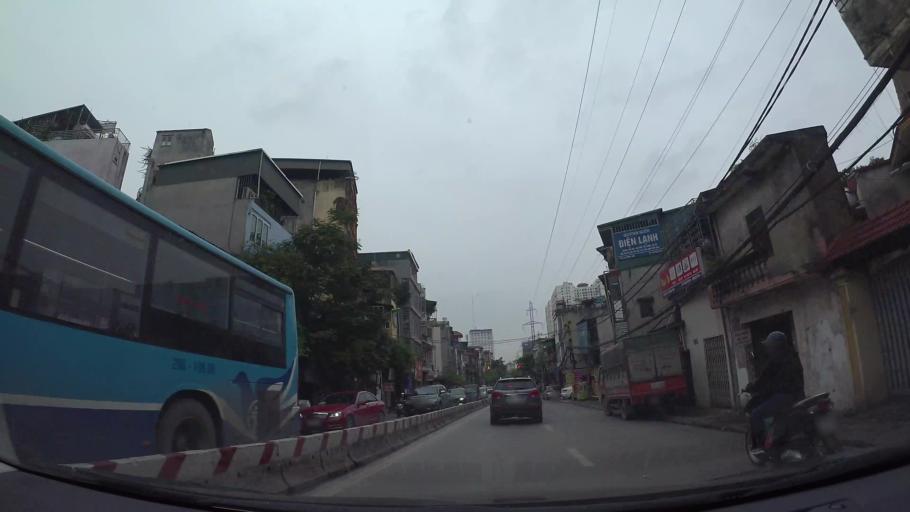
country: VN
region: Ha Noi
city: Hai BaTrung
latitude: 21.0051
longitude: 105.8690
